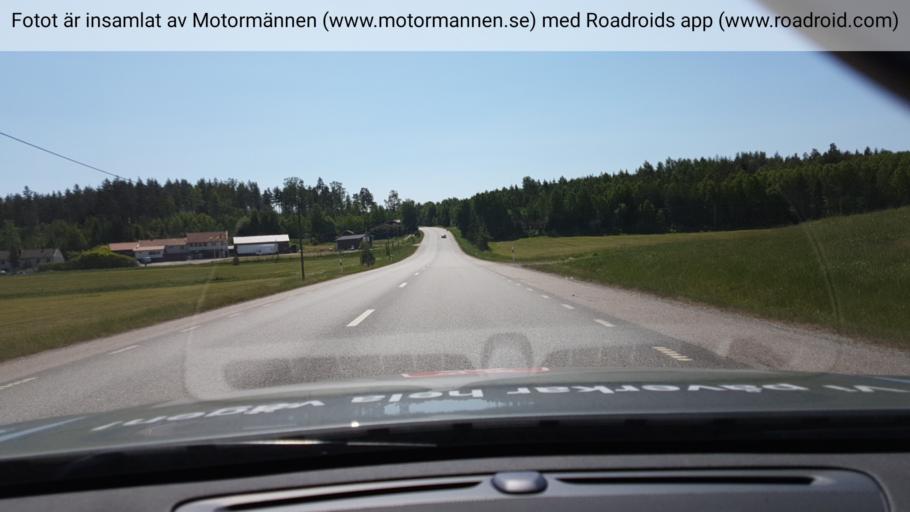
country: SE
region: Stockholm
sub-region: Norrtalje Kommun
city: Rimbo
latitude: 59.6465
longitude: 18.3330
